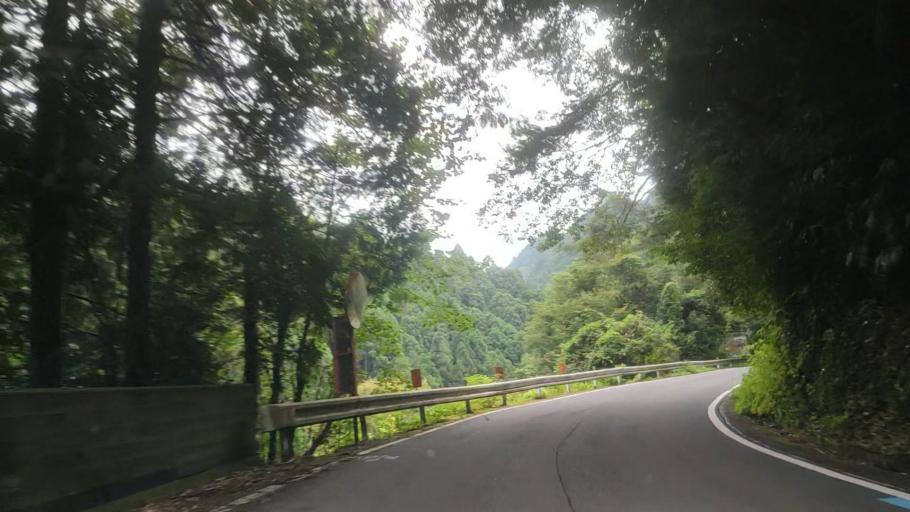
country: JP
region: Wakayama
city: Koya
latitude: 34.2541
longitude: 135.5454
